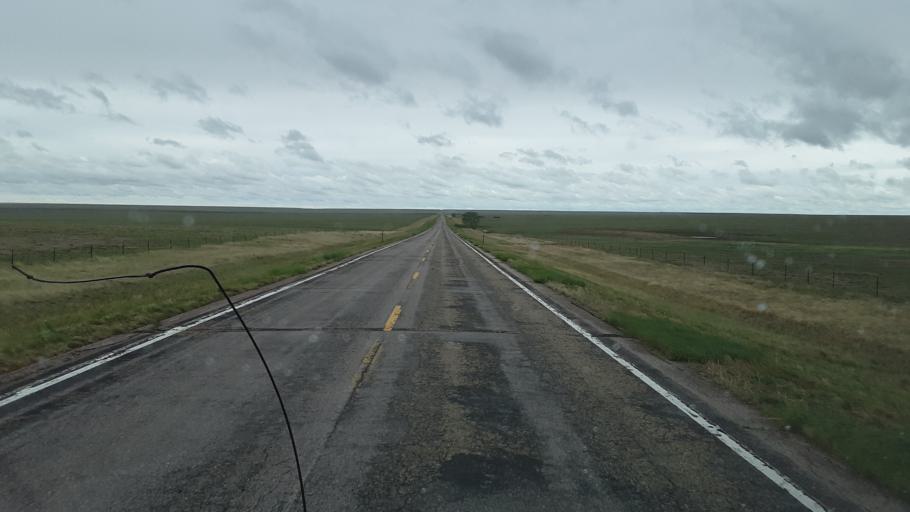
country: US
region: Colorado
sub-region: Lincoln County
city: Hugo
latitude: 38.8498
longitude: -103.3196
